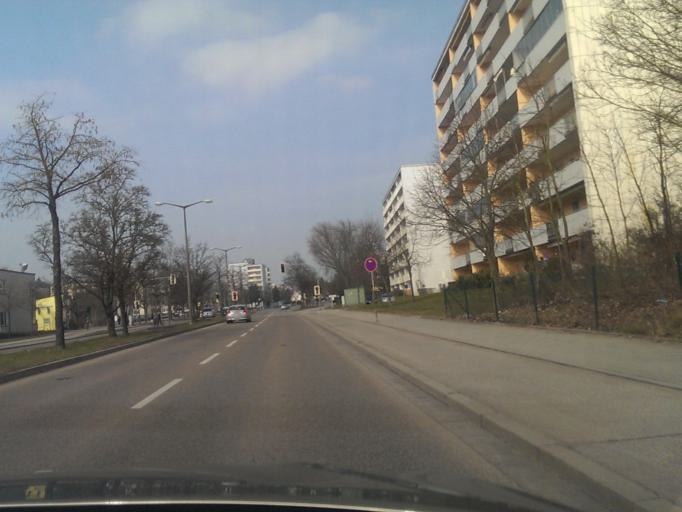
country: DE
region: Bavaria
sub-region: Upper Palatinate
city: Regensburg
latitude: 49.0315
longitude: 12.1239
